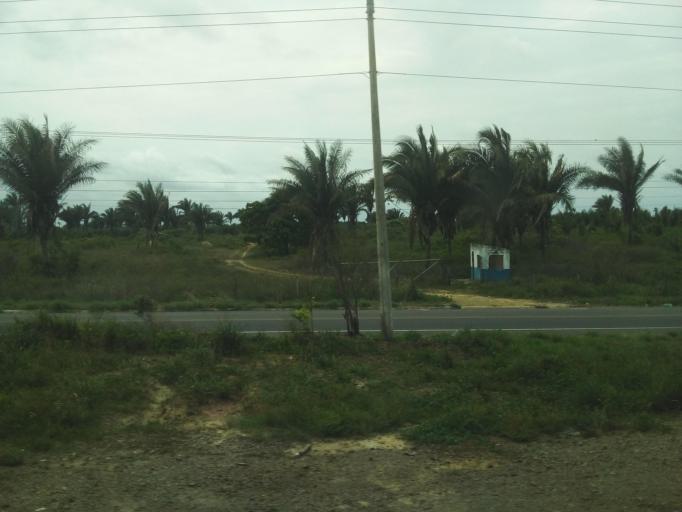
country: BR
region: Maranhao
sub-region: Santa Ines
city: Santa Ines
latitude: -3.6755
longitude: -45.8778
